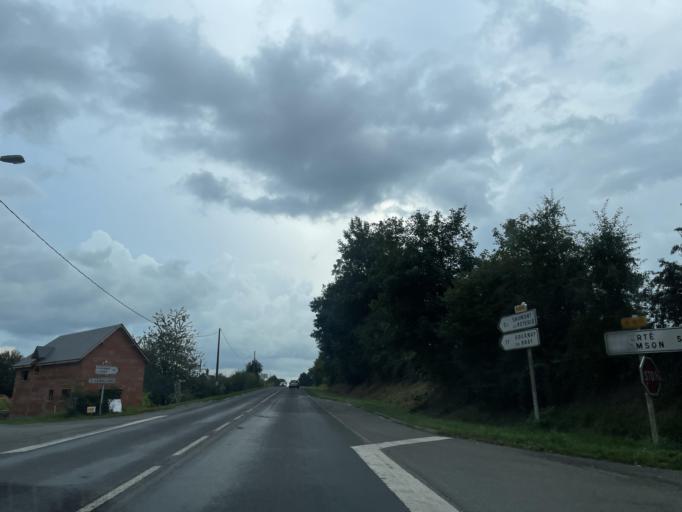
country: FR
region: Haute-Normandie
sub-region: Departement de la Seine-Maritime
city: Forges-les-Eaux
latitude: 49.5956
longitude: 1.5828
